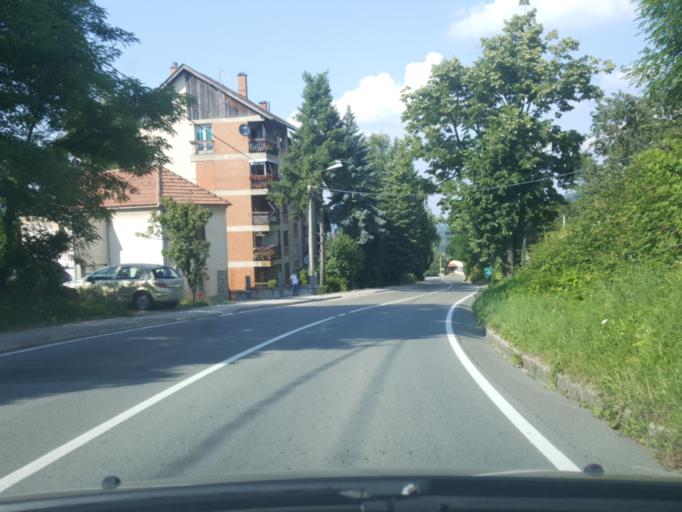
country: RS
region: Central Serbia
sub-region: Moravicki Okrug
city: Gornji Milanovac
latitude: 44.1381
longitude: 20.4928
